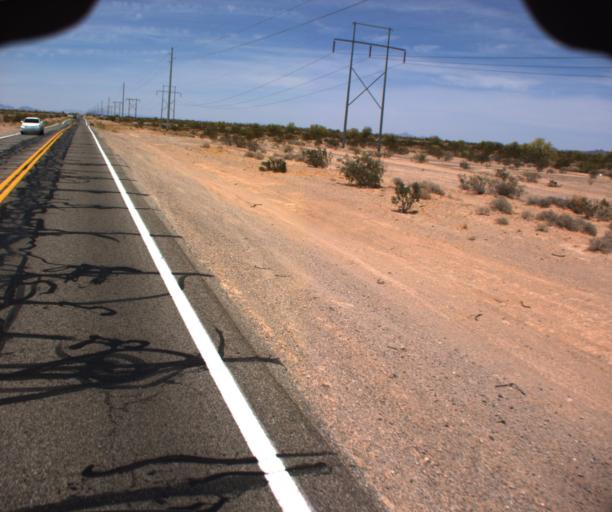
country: US
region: Arizona
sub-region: La Paz County
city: Quartzsite
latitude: 33.8182
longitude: -114.2170
